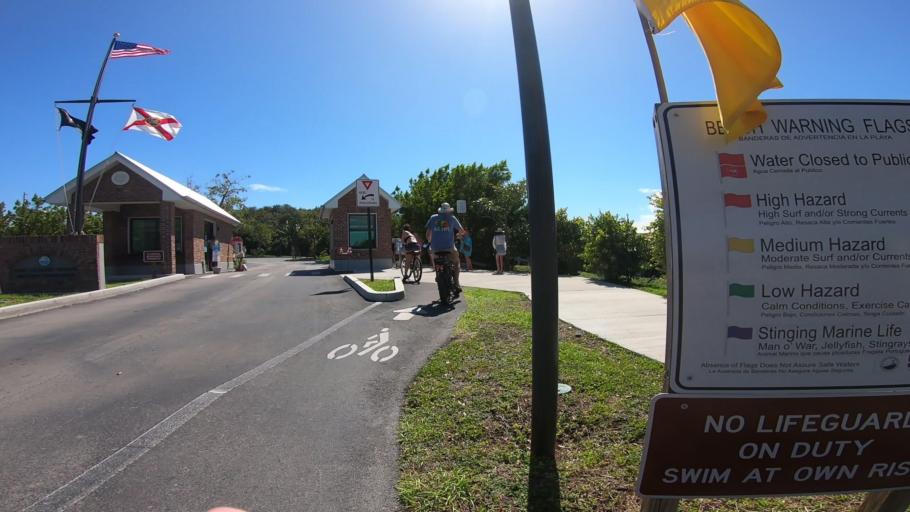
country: US
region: Florida
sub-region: Monroe County
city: Key West
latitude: 24.5482
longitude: -81.8087
